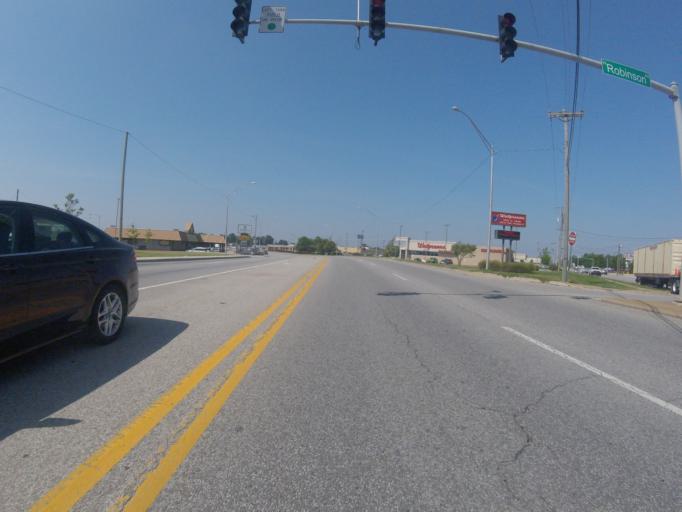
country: US
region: Arkansas
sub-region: Washington County
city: Springdale
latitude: 36.1672
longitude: -94.1416
